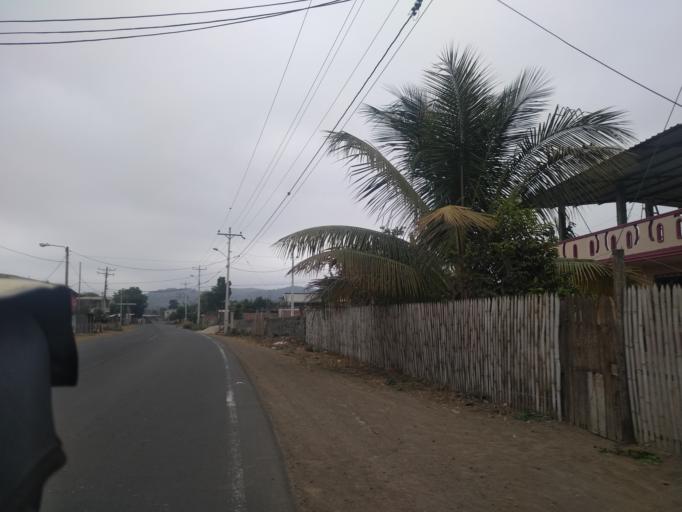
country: EC
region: Manabi
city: Montecristi
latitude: -1.0778
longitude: -80.6713
